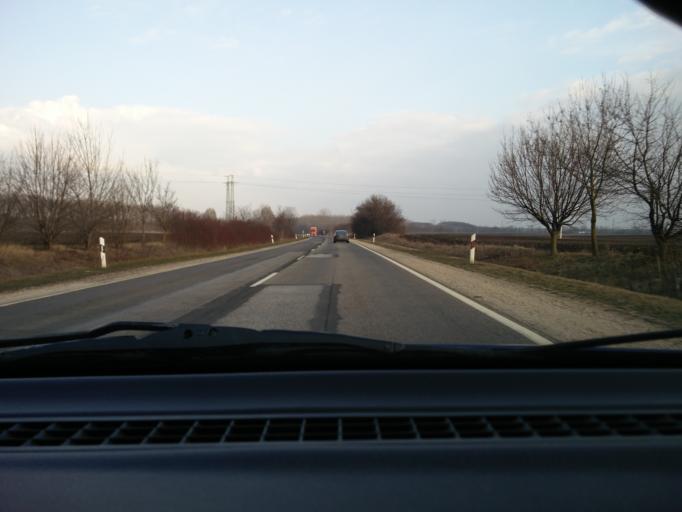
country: HU
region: Pest
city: Pilis
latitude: 47.2568
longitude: 19.5497
